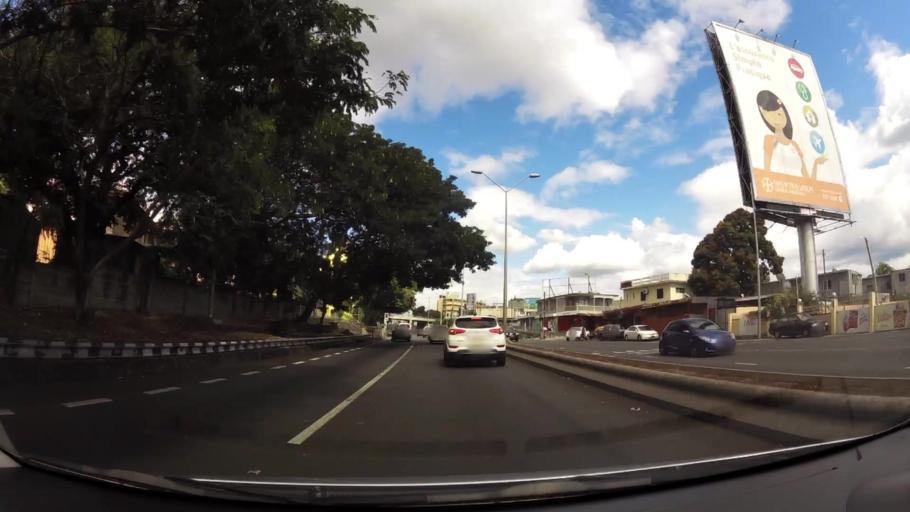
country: MU
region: Port Louis
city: Port Louis
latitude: -20.1667
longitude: 57.4857
